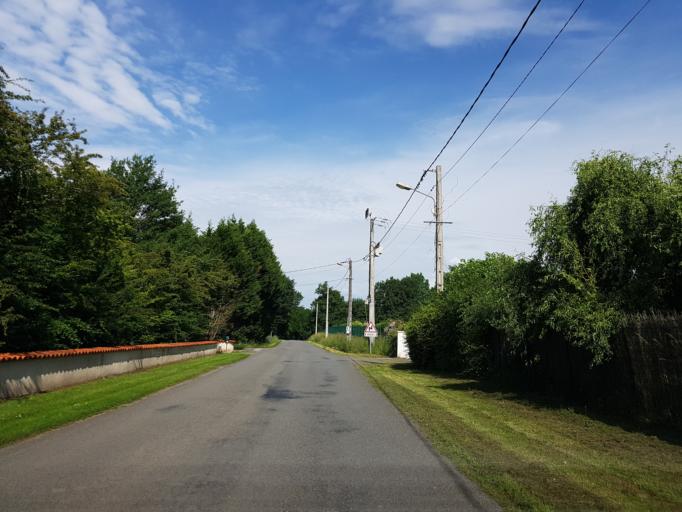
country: FR
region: Poitou-Charentes
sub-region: Departement de la Charente
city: Chabanais
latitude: 45.8837
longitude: 0.7073
